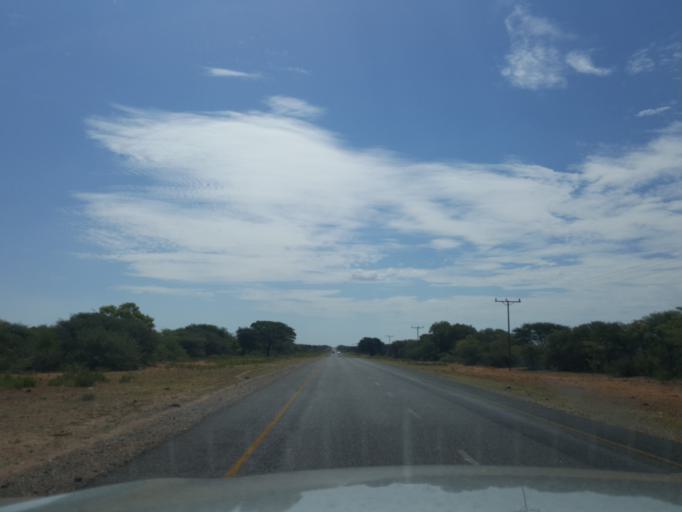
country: BW
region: Kweneng
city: Letlhakeng
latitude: -24.1603
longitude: 25.1670
